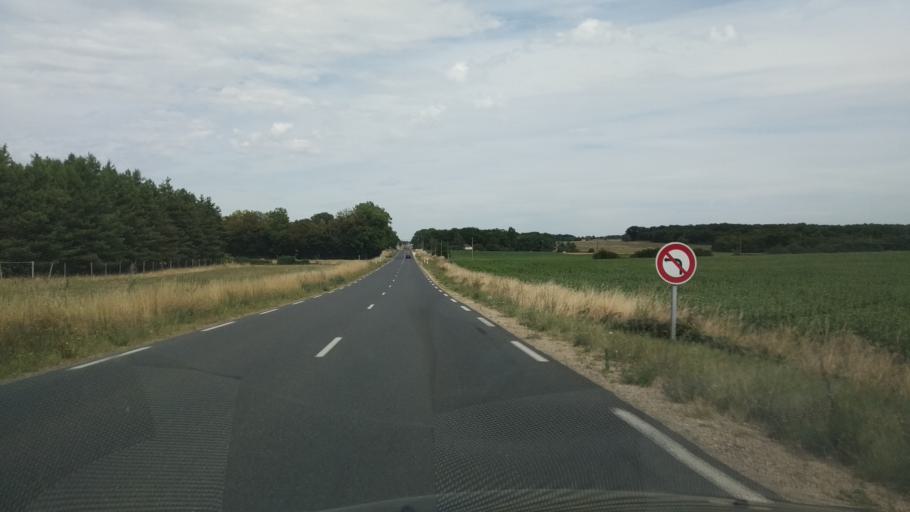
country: FR
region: Poitou-Charentes
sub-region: Departement de la Vienne
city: Sevres-Anxaumont
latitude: 46.5588
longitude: 0.4684
